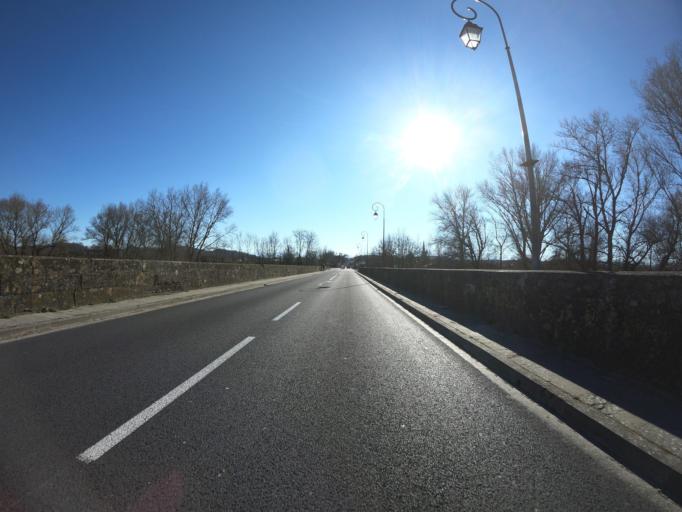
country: FR
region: Midi-Pyrenees
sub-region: Departement de l'Ariege
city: Mirepoix
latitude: 43.0934
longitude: 1.8762
